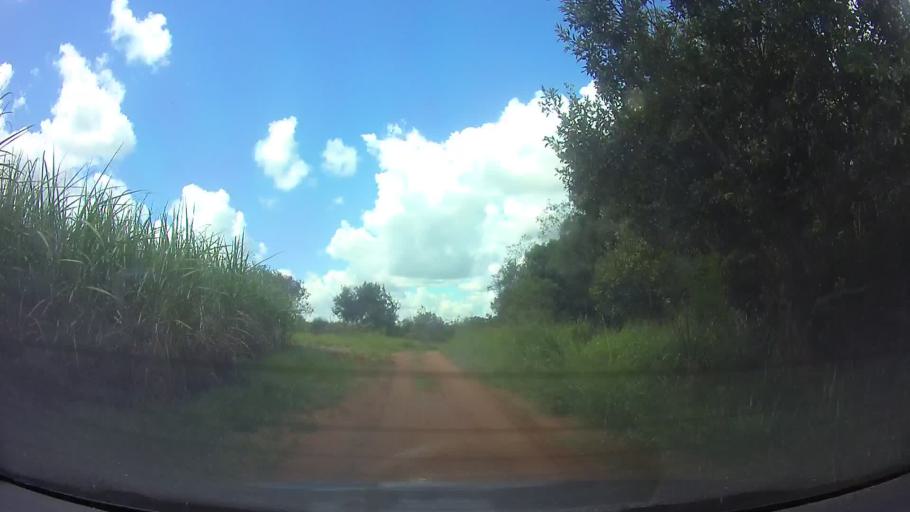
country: PY
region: Paraguari
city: La Colmena
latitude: -25.9723
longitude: -56.7306
